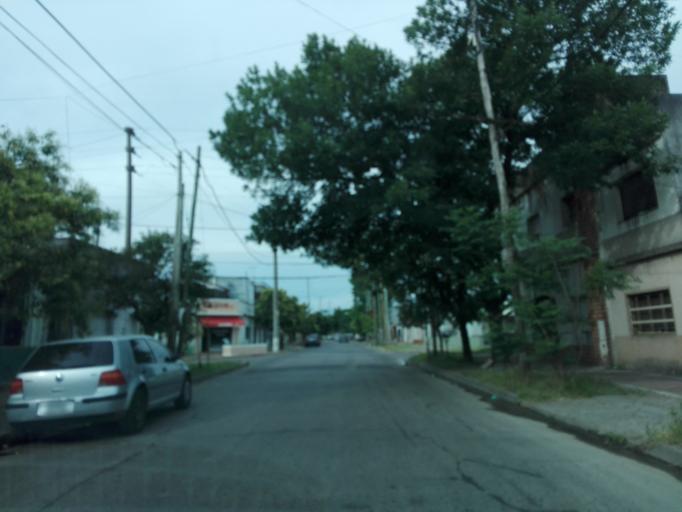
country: AR
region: Buenos Aires
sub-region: Partido de Lanus
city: Lanus
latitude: -34.7236
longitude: -58.3867
